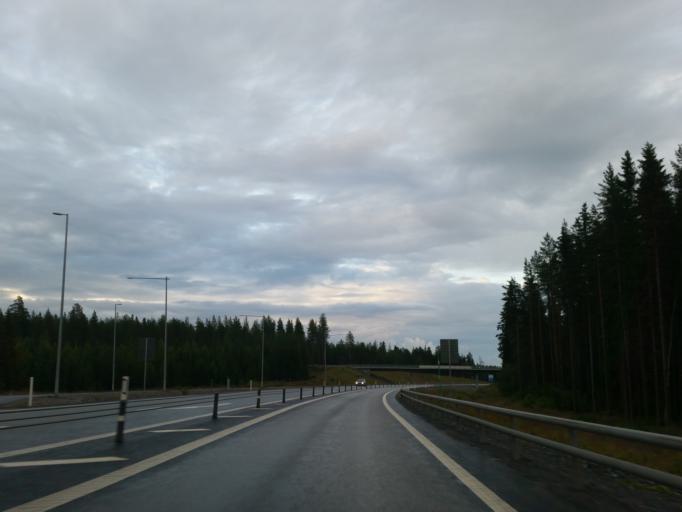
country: SE
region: Vaesterbotten
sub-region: Umea Kommun
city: Umea
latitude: 63.8538
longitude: 20.2818
